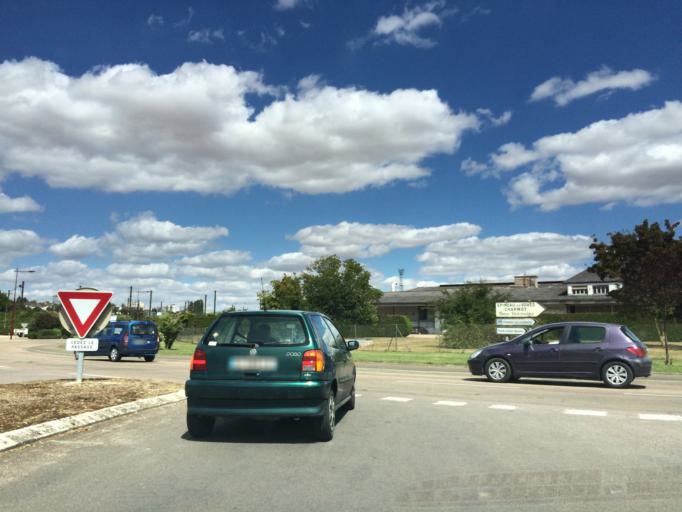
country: FR
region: Bourgogne
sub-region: Departement de l'Yonne
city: Migennes
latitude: 47.9583
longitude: 3.5039
